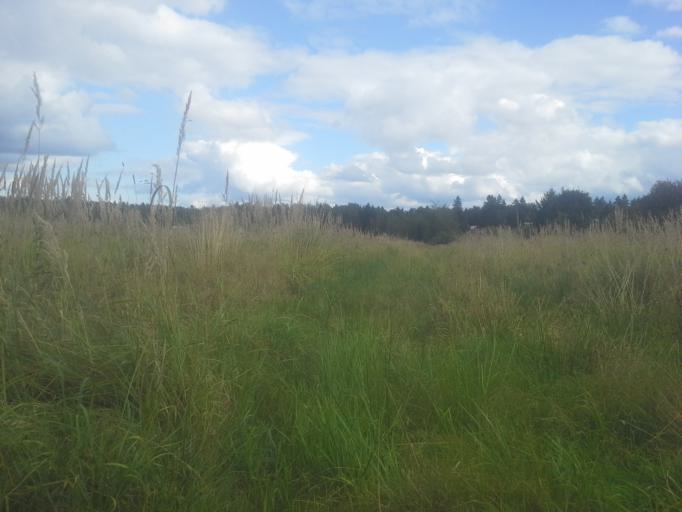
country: RU
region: Moskovskaya
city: Kievskij
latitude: 55.3525
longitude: 36.9595
